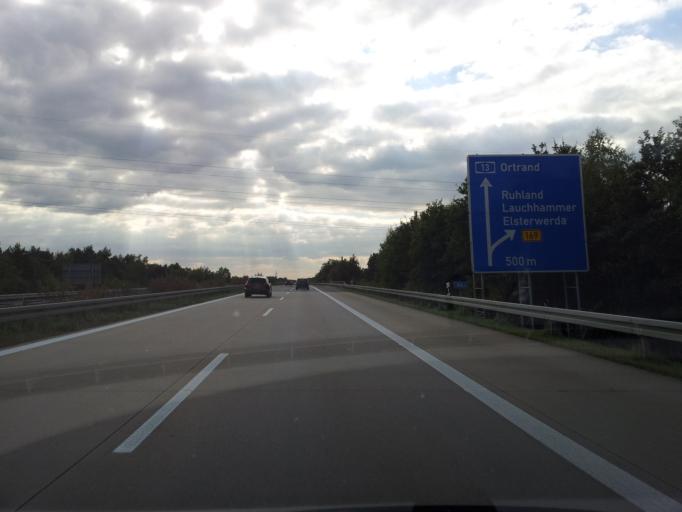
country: DE
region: Brandenburg
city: Schwarzheide
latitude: 51.4763
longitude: 13.8714
